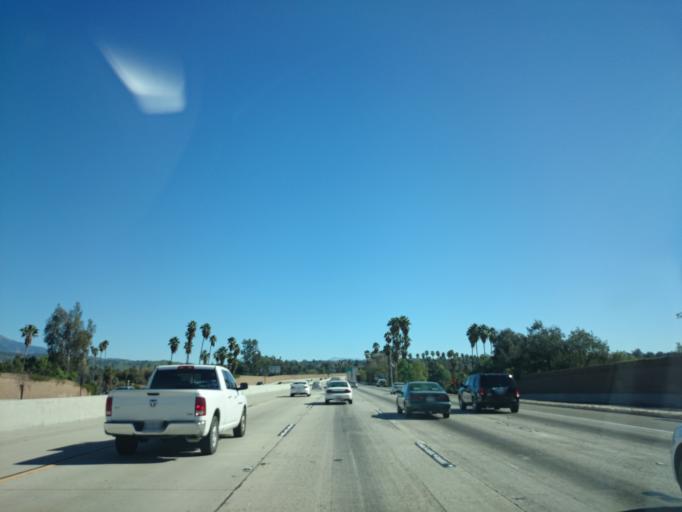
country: US
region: California
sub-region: San Bernardino County
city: Redlands
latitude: 34.0576
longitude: -117.1691
